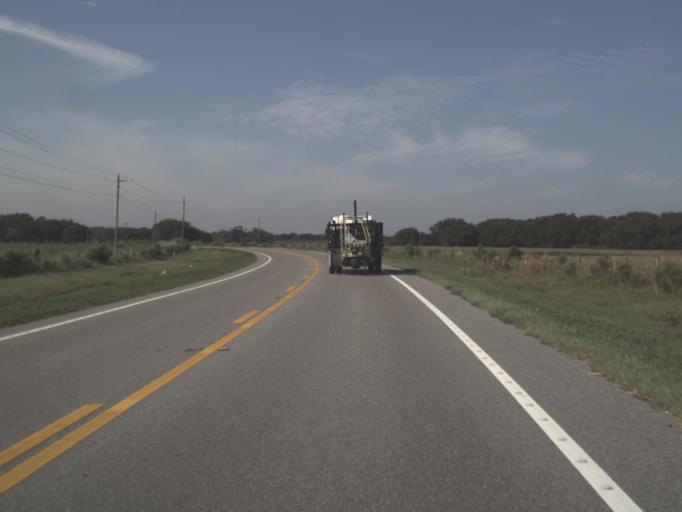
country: US
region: Florida
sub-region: Highlands County
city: Avon Park
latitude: 27.5869
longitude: -81.6005
